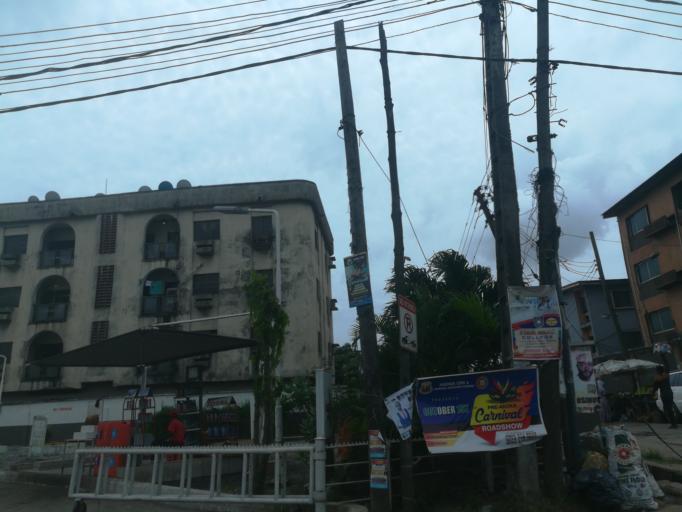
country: NG
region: Lagos
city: Somolu
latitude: 6.5281
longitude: 3.3868
